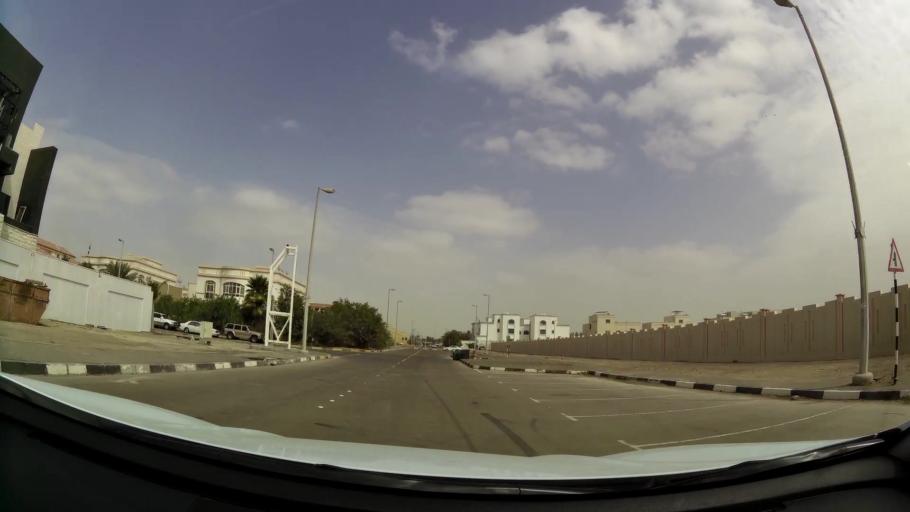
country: AE
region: Abu Dhabi
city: Abu Dhabi
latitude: 24.3942
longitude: 54.4964
